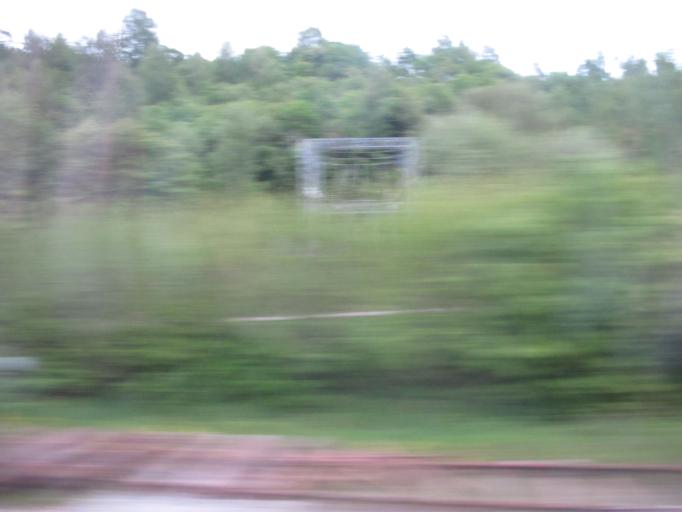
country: NO
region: Oppland
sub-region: Lillehammer
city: Lillehammer
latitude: 61.1620
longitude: 10.4054
